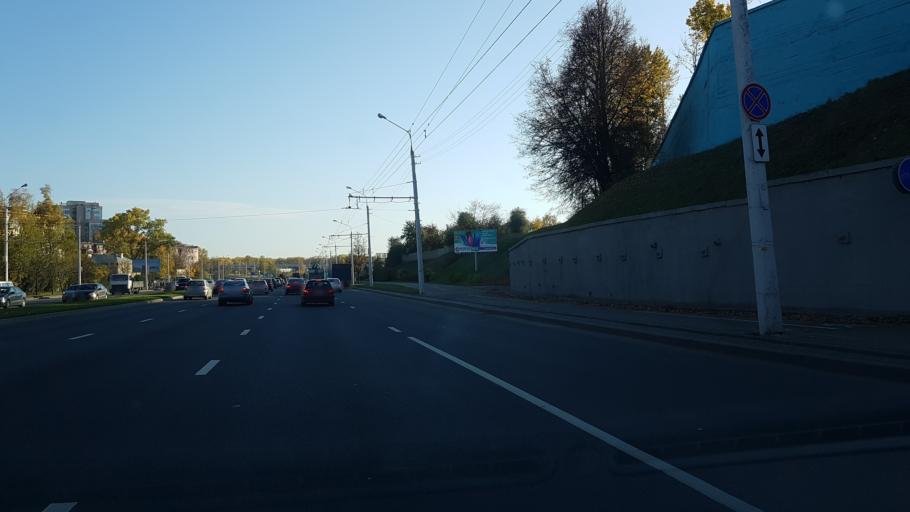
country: BY
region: Minsk
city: Novoye Medvezhino
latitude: 53.8892
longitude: 27.5007
